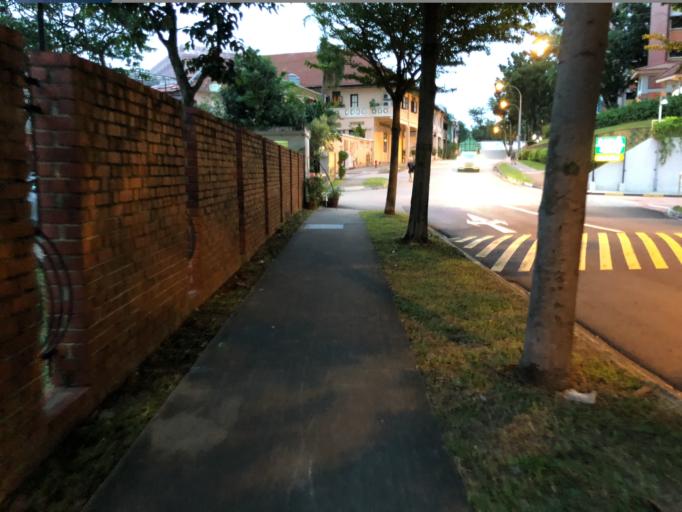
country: SG
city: Singapore
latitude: 1.2760
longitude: 103.8386
